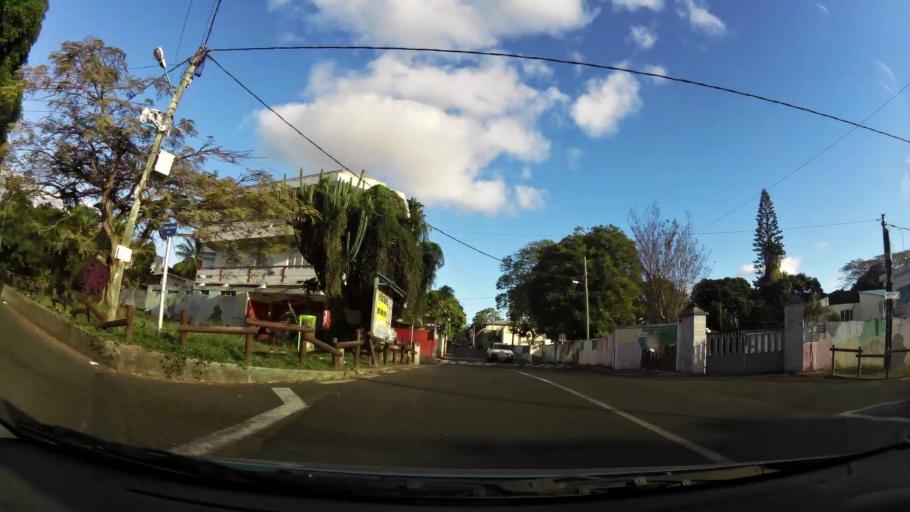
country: MU
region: Moka
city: Moka
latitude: -20.2239
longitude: 57.4636
